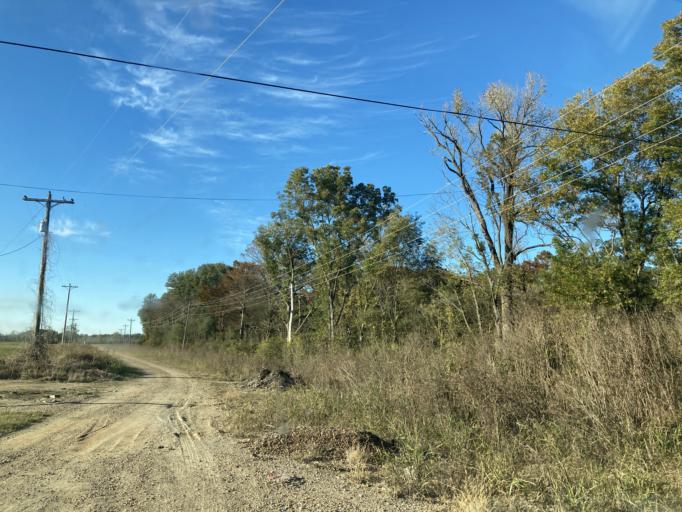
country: US
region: Mississippi
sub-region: Yazoo County
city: Yazoo City
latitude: 32.8831
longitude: -90.4204
